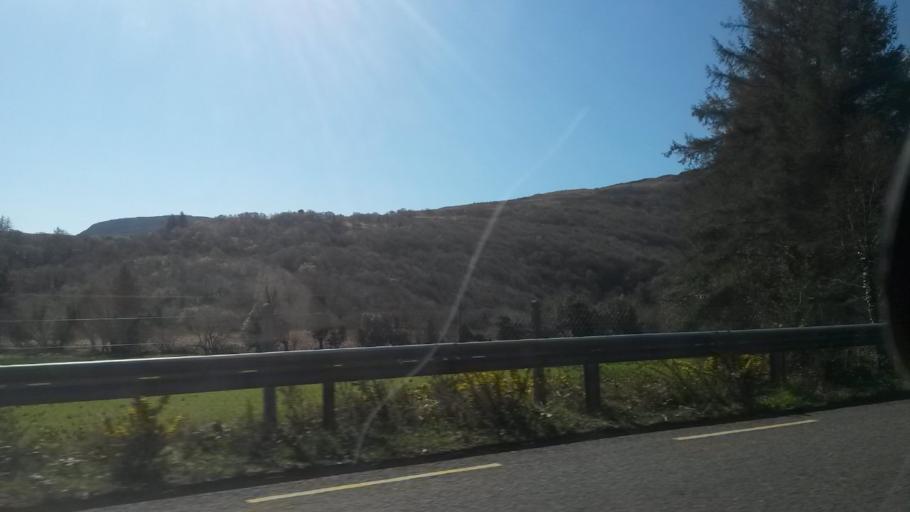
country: IE
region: Munster
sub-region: Ciarrai
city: Cill Airne
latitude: 51.9650
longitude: -9.3583
